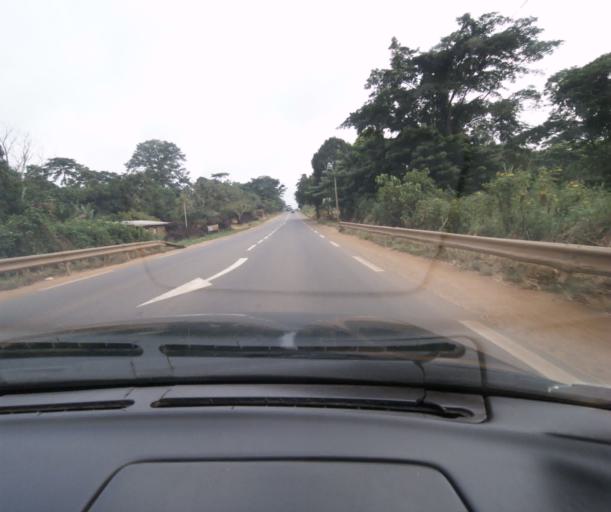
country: CM
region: Centre
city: Obala
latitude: 4.0867
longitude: 11.5456
